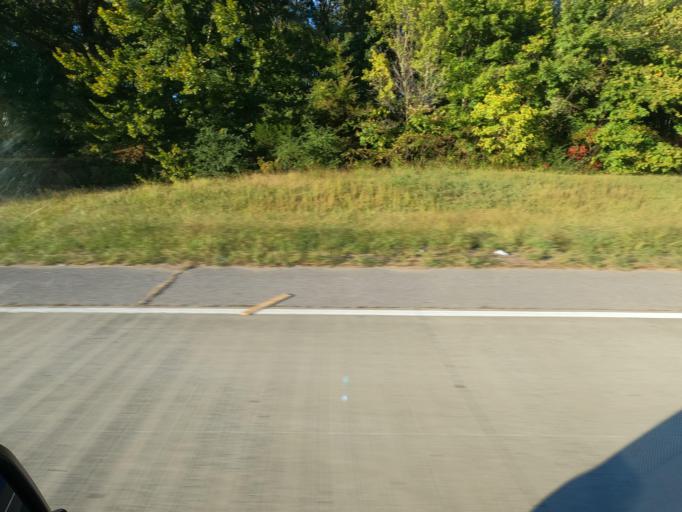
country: US
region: Tennessee
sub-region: Shelby County
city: Lakeland
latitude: 35.3107
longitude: -89.7684
